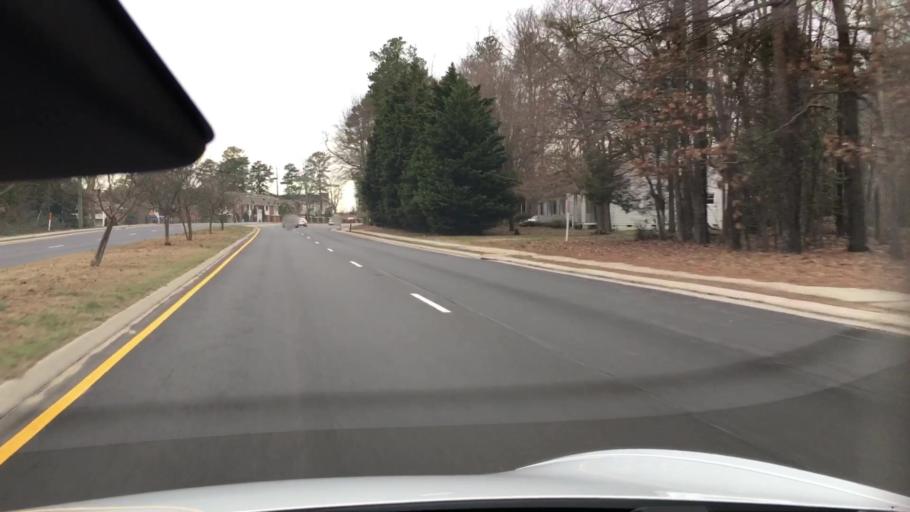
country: US
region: Virginia
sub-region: Chesterfield County
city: Bon Air
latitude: 37.5183
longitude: -77.6008
